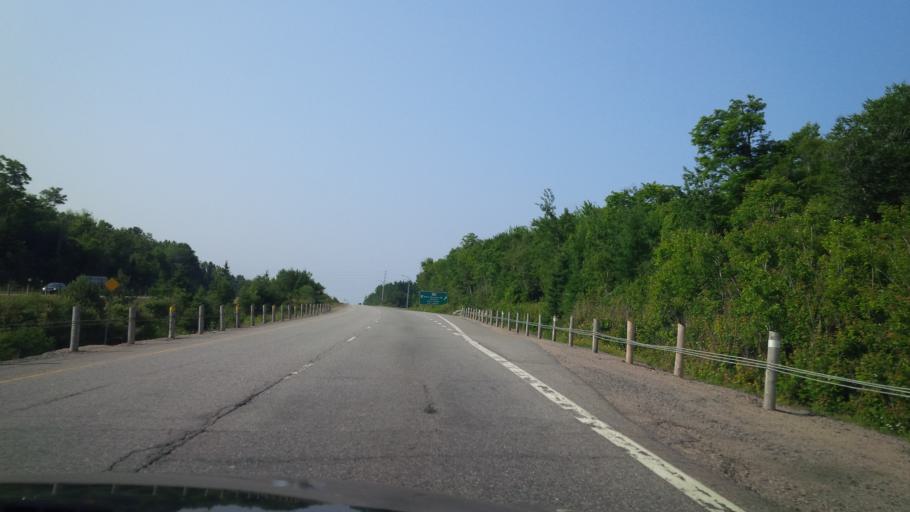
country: CA
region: Ontario
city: Huntsville
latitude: 45.2203
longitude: -79.3135
